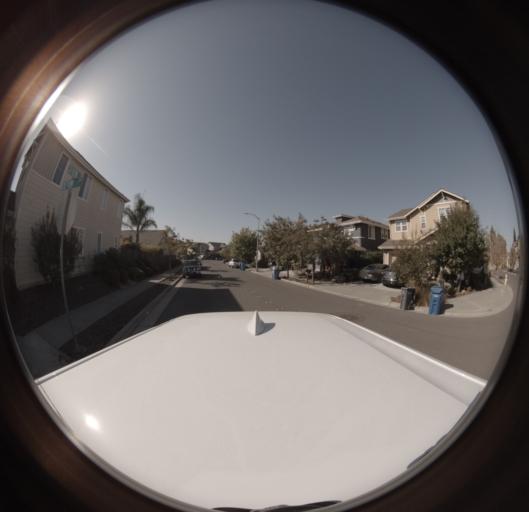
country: US
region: California
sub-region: Sonoma County
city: Petaluma
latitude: 38.2360
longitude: -122.5913
